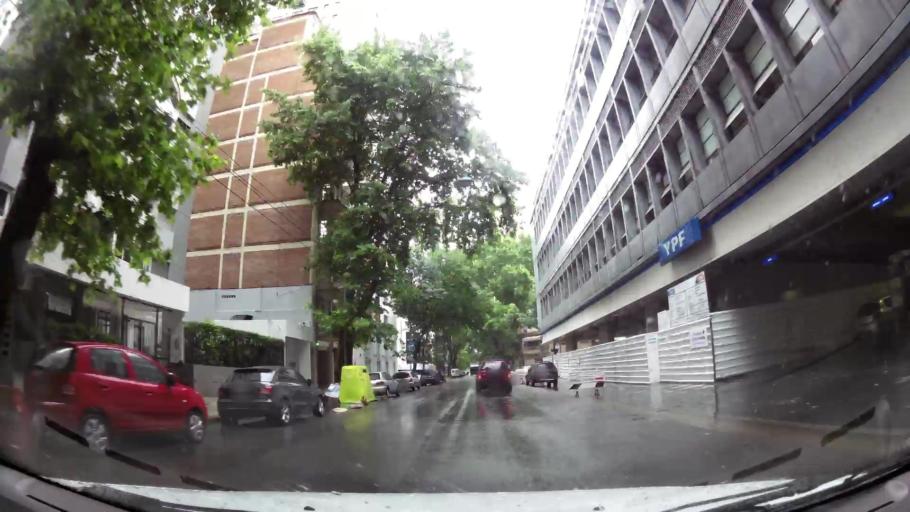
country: AR
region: Buenos Aires F.D.
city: Colegiales
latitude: -34.5742
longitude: -58.4216
